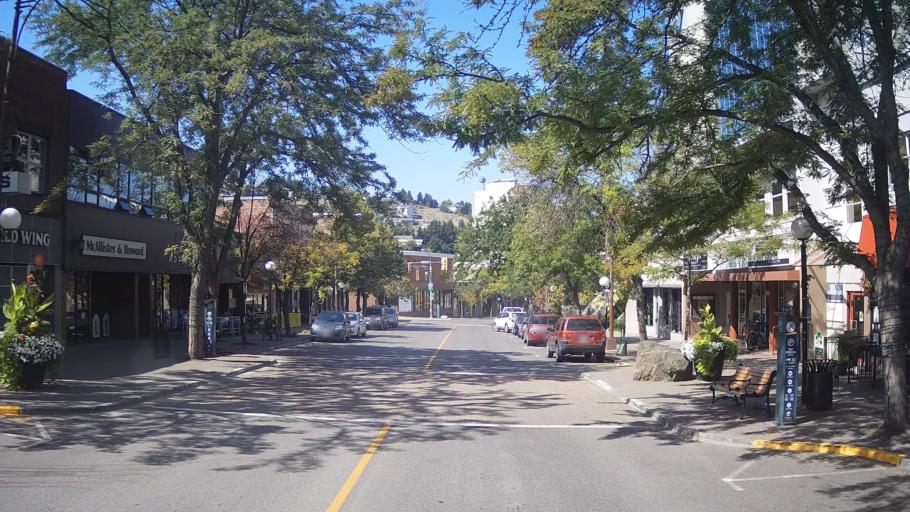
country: CA
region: British Columbia
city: Kamloops
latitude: 50.6756
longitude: -120.3356
